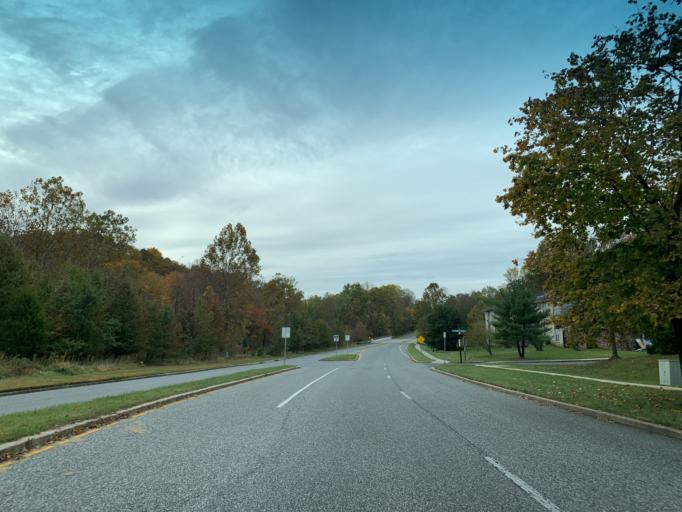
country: US
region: Maryland
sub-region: Harford County
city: South Bel Air
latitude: 39.5391
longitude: -76.3246
